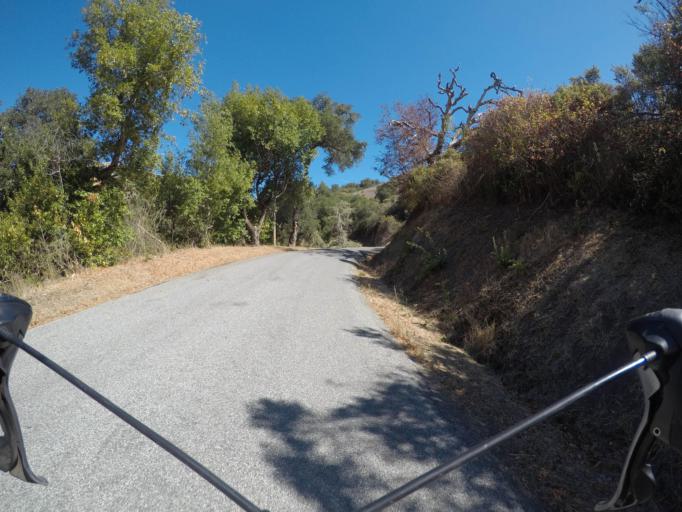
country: US
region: California
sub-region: San Mateo County
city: Portola Valley
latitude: 37.3616
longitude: -122.2536
